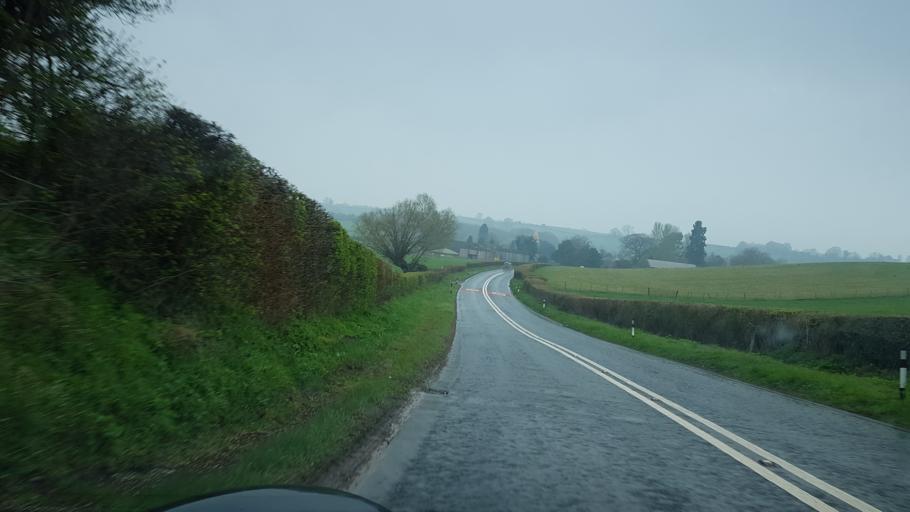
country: GB
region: England
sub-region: Herefordshire
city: Moreton Jeffries
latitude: 52.1465
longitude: -2.5539
